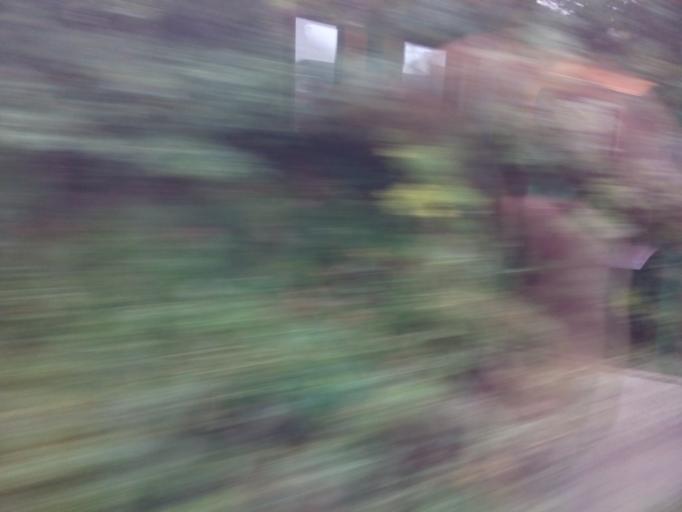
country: GB
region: England
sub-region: City and Borough of Leeds
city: Scholes
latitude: 53.8040
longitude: -1.4564
